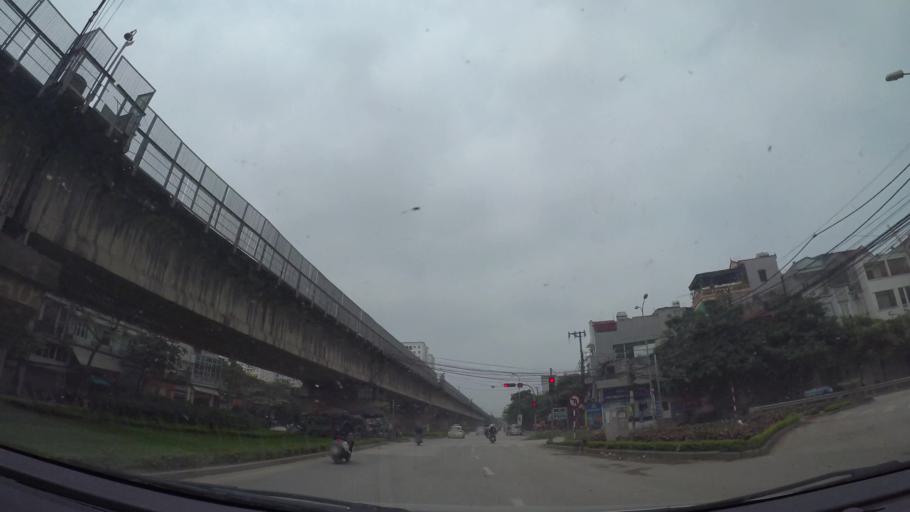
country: VN
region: Ha Noi
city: Tay Ho
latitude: 21.0807
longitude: 105.7856
